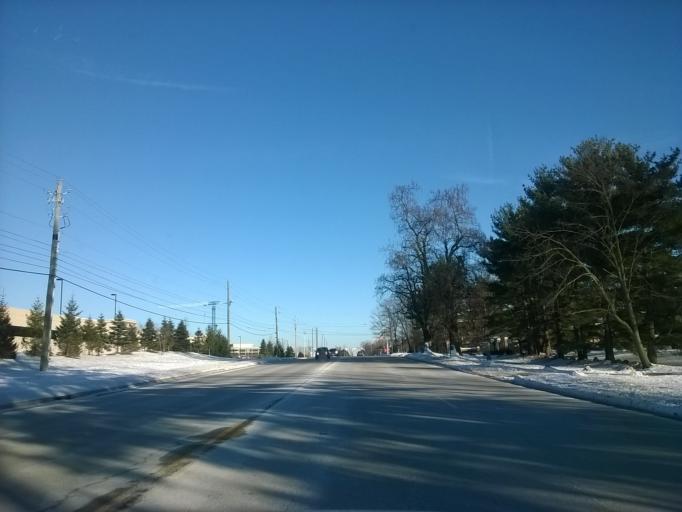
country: US
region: Indiana
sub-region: Marion County
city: Meridian Hills
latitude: 39.9270
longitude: -86.1619
